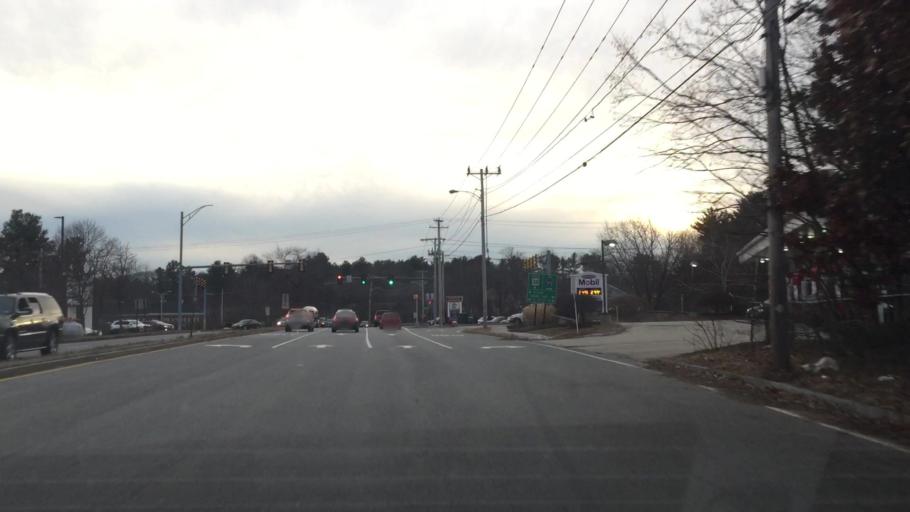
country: US
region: New Hampshire
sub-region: Rockingham County
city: Salem
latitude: 42.7672
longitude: -71.2336
